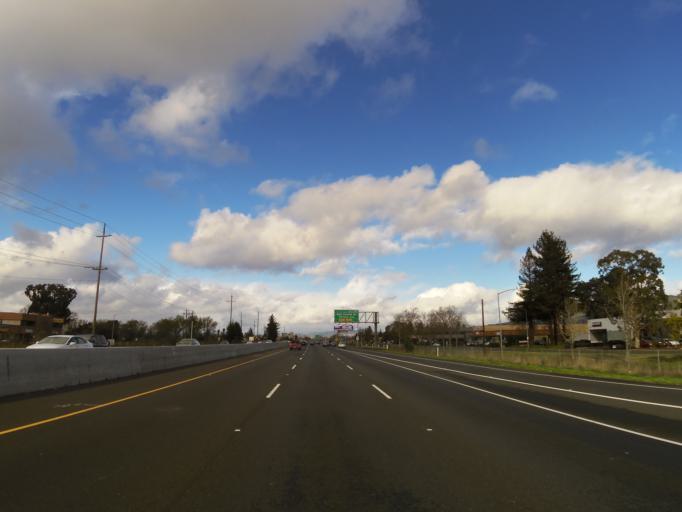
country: US
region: California
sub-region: Sonoma County
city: Rohnert Park
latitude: 38.3542
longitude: -122.7130
